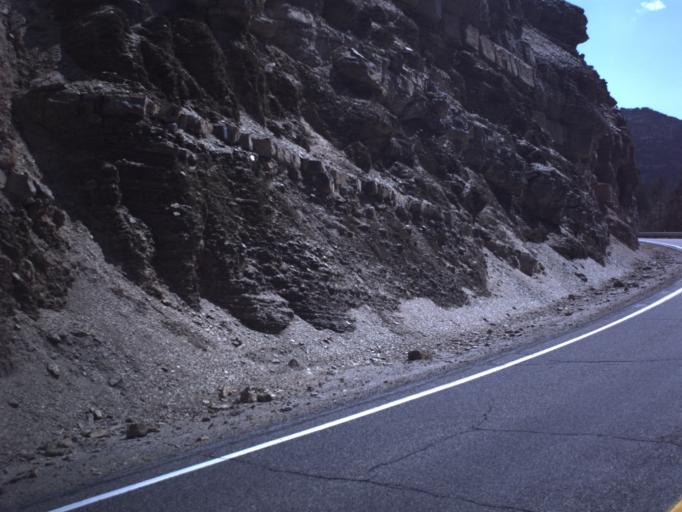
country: US
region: Idaho
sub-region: Bear Lake County
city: Paris
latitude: 41.9518
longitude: -111.4954
